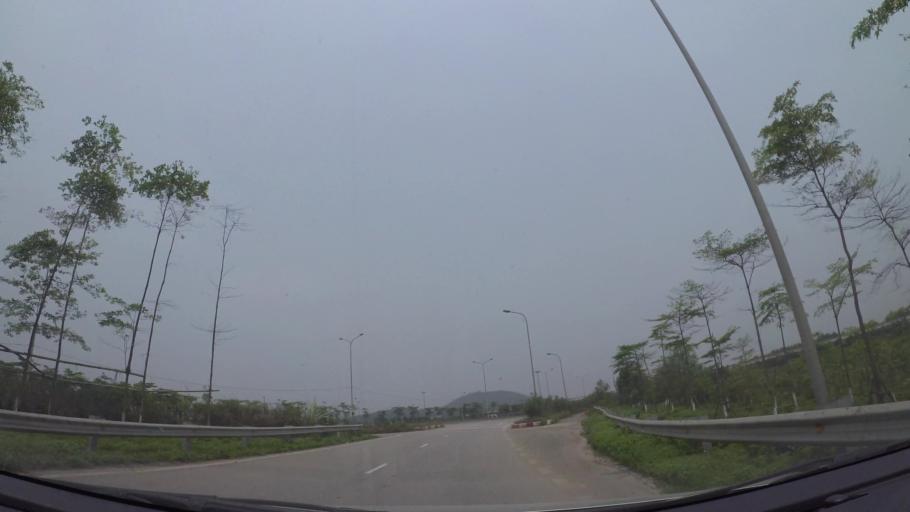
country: VN
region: Ha Noi
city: Lien Quan
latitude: 20.9883
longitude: 105.5258
